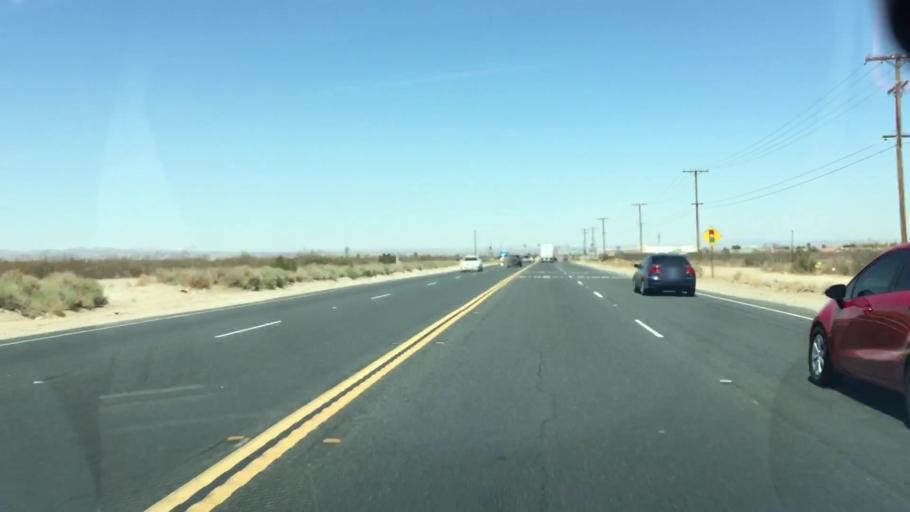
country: US
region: California
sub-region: San Bernardino County
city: Mountain View Acres
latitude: 34.4666
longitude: -117.3995
